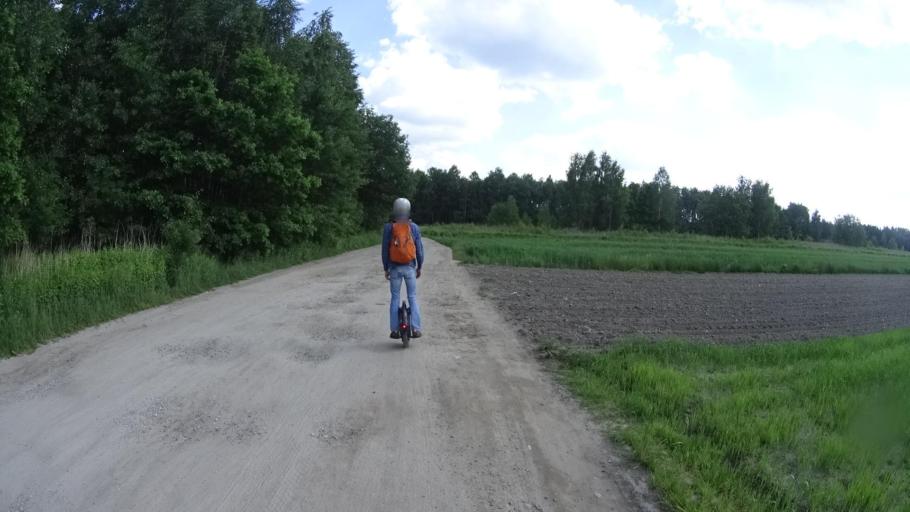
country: PL
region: Masovian Voivodeship
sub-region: Warszawa
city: Kabaty
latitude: 52.1107
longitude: 21.0883
